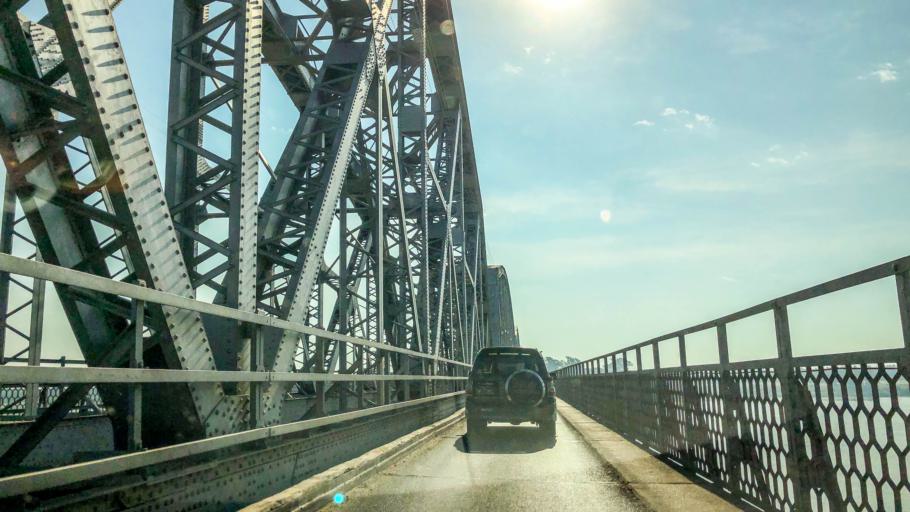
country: MM
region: Sagain
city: Sagaing
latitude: 21.8731
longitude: 95.9900
